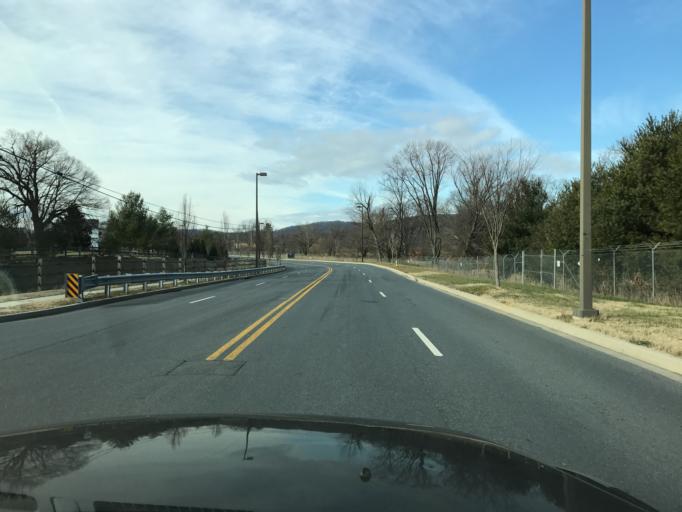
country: US
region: Maryland
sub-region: Frederick County
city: Clover Hill
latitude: 39.4304
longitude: -77.4487
